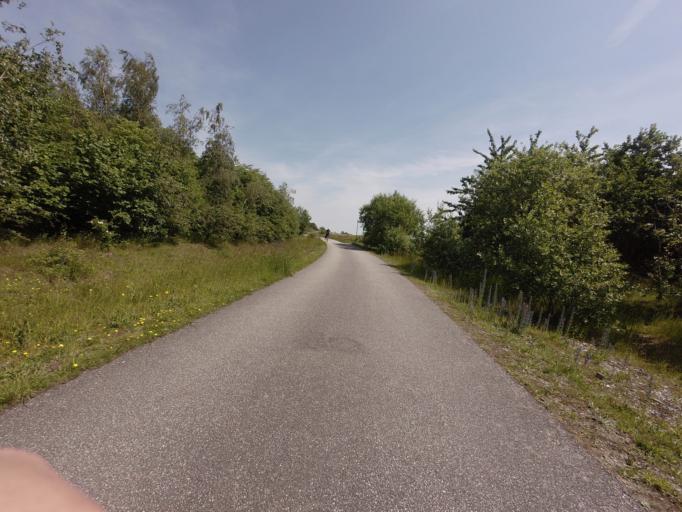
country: SE
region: Skane
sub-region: Malmo
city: Bunkeflostrand
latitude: 55.5675
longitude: 12.9070
